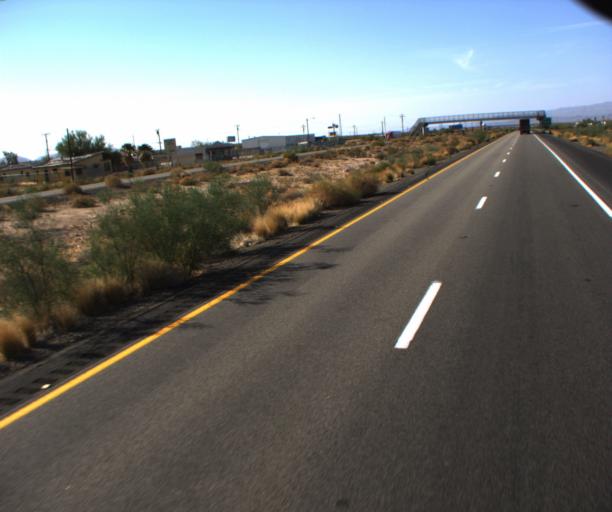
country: US
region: Arizona
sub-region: Mohave County
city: Kingman
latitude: 34.8748
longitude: -114.1480
